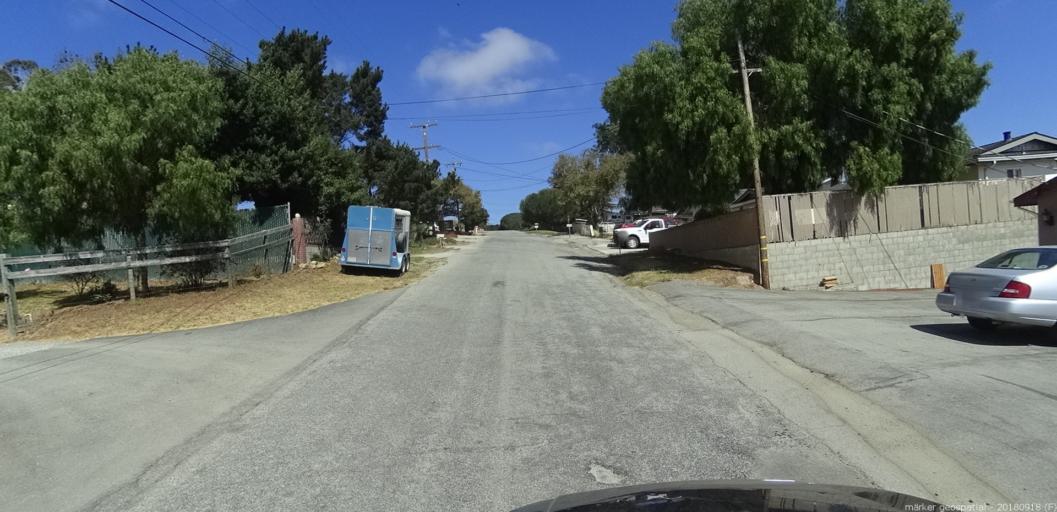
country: US
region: California
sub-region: Monterey County
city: Prunedale
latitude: 36.7780
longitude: -121.6632
